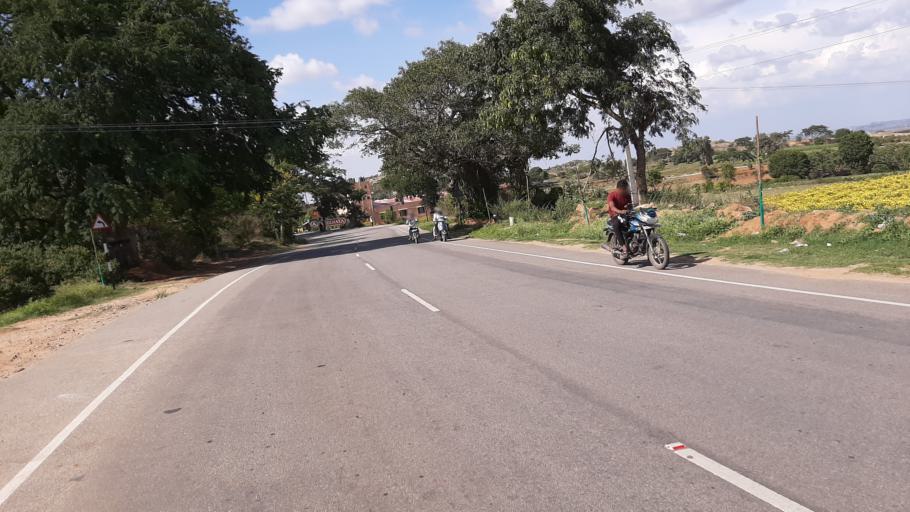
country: IN
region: Tamil Nadu
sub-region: Krishnagiri
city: Denkanikota
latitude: 12.5500
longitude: 77.7860
